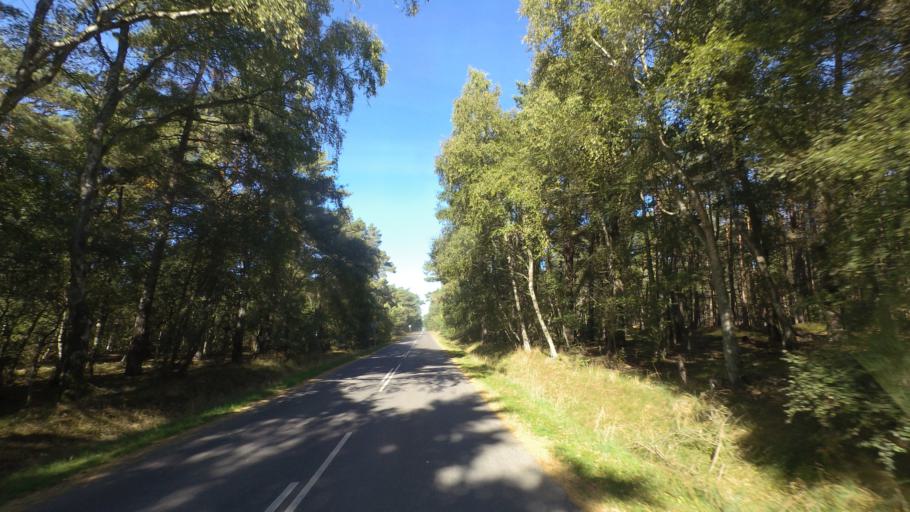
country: DK
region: Capital Region
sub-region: Bornholm Kommune
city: Nexo
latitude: 54.9978
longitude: 15.0763
